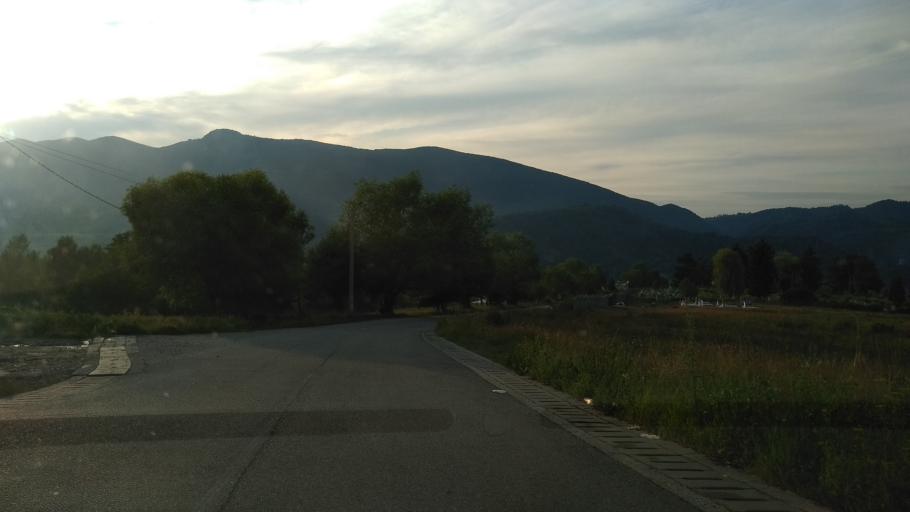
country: RO
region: Hunedoara
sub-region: Municipiul  Vulcan
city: Jiu-Paroseni
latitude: 45.3647
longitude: 23.2847
